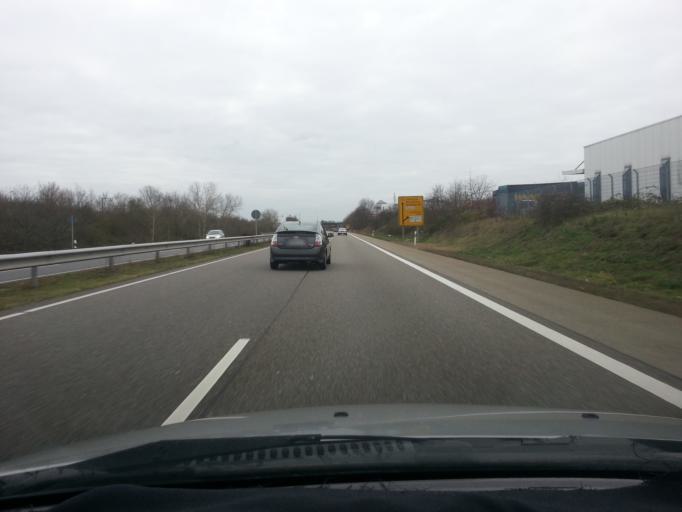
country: DE
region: Baden-Wuerttemberg
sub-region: Karlsruhe Region
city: Hockenheim
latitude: 49.3295
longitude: 8.5427
